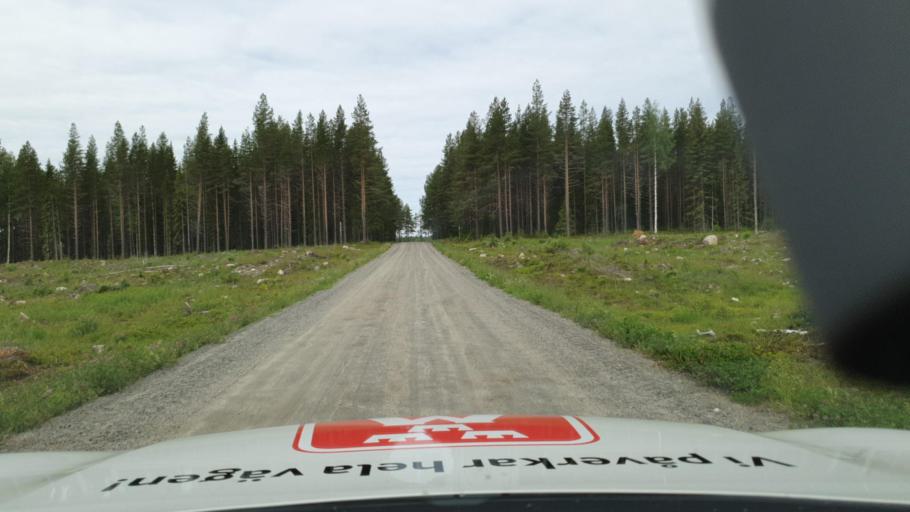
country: SE
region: Vaesterbotten
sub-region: Skelleftea Kommun
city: Langsele
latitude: 64.4765
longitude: 20.2153
